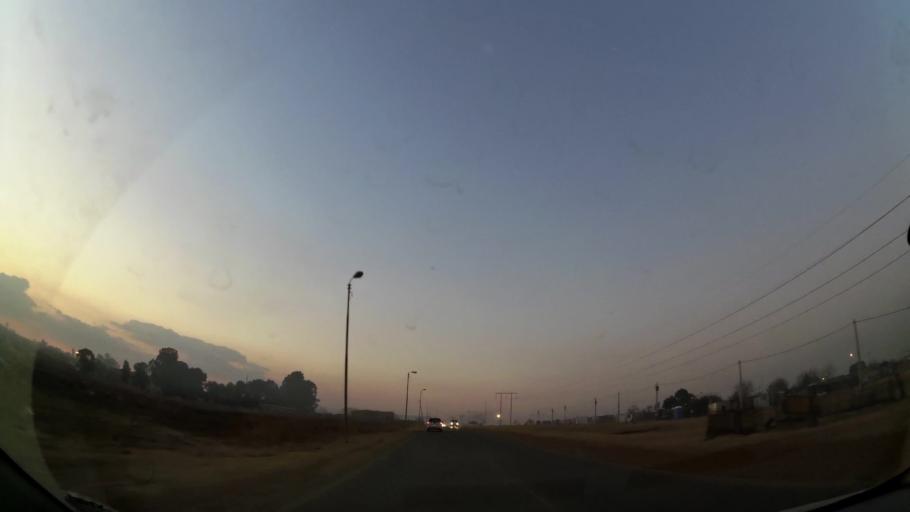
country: ZA
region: Gauteng
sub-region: Ekurhuleni Metropolitan Municipality
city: Springs
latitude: -26.3069
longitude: 28.3796
